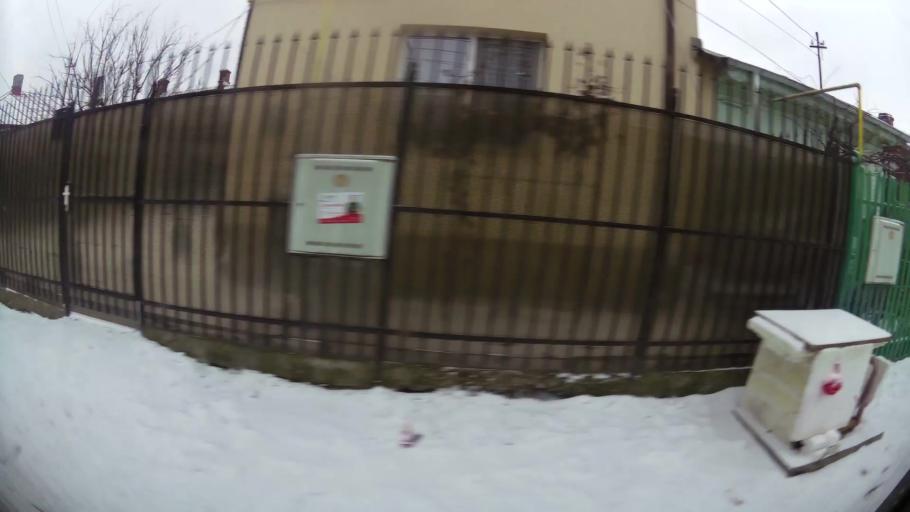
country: RO
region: Prahova
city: Ploiesti
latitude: 44.9268
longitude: 26.0148
